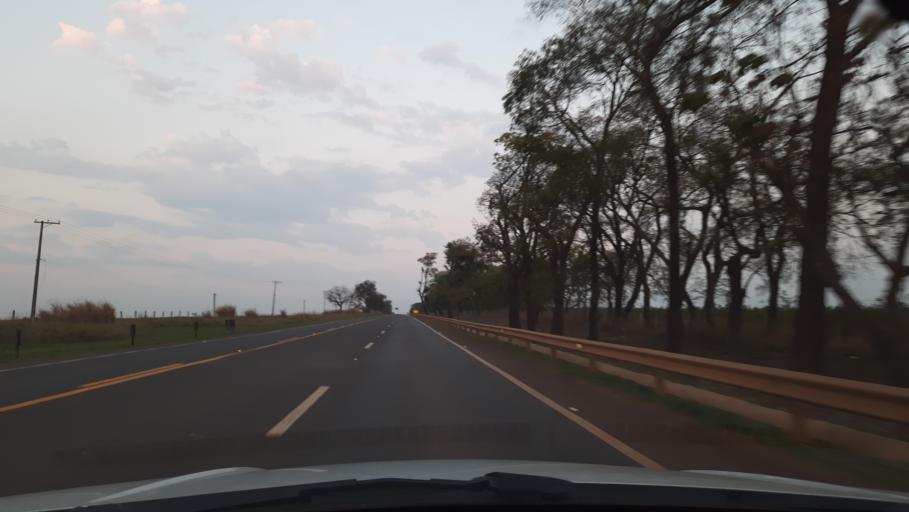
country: BR
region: Sao Paulo
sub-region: Santa Cruz Das Palmeiras
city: Santa Cruz das Palmeiras
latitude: -21.8070
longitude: -47.1814
